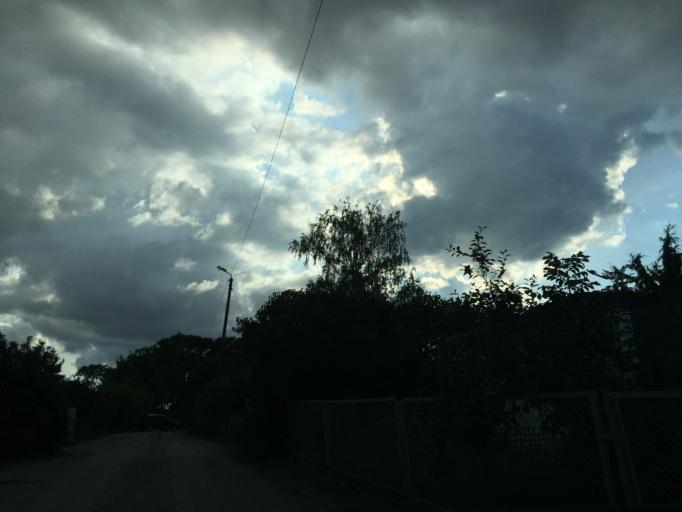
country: LT
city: Zagare
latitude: 56.3644
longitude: 23.2599
